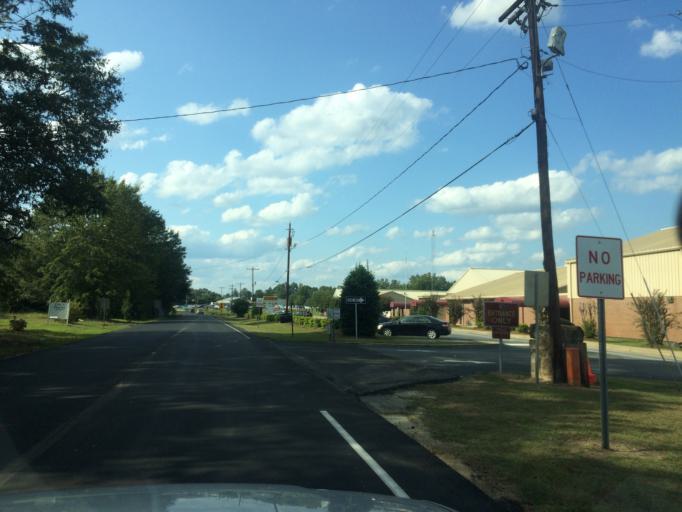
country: US
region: South Carolina
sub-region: Greenwood County
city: Ware Shoals
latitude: 34.5181
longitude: -82.1873
